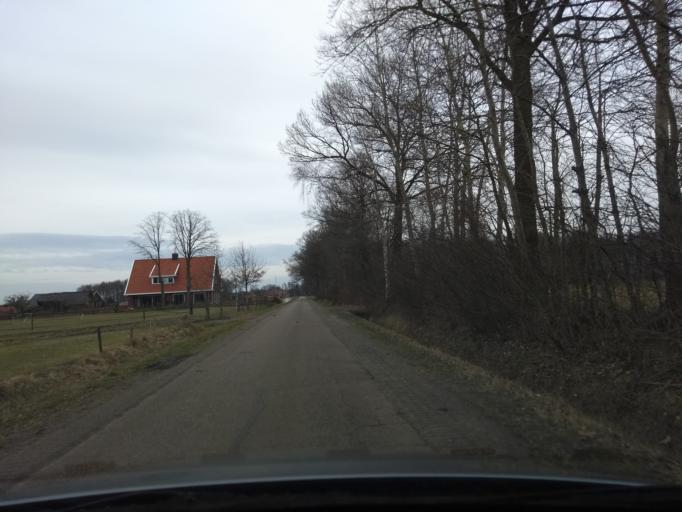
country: NL
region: Overijssel
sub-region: Gemeente Borne
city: Borne
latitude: 52.3463
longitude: 6.7333
